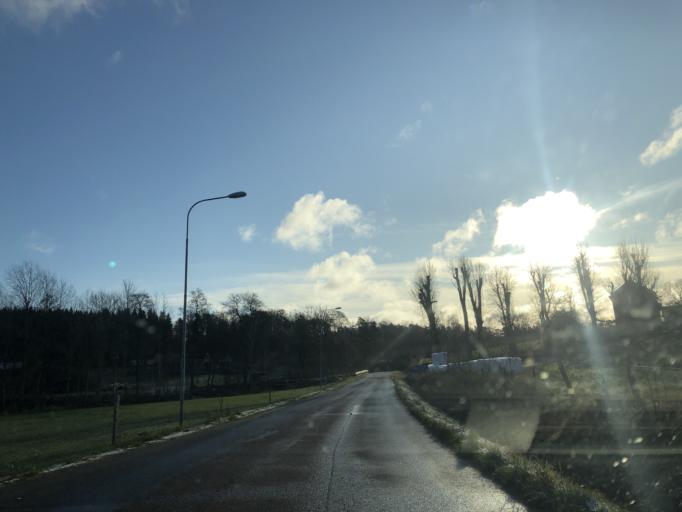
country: SE
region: Vaestra Goetaland
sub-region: Ulricehamns Kommun
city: Ulricehamn
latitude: 57.7465
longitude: 13.4166
